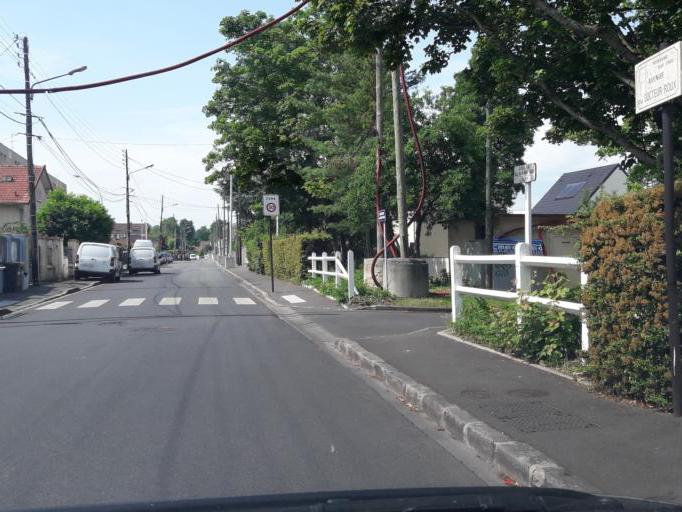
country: FR
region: Ile-de-France
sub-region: Departement de l'Essonne
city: Morsang-sur-Orge
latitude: 48.6572
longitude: 2.3496
